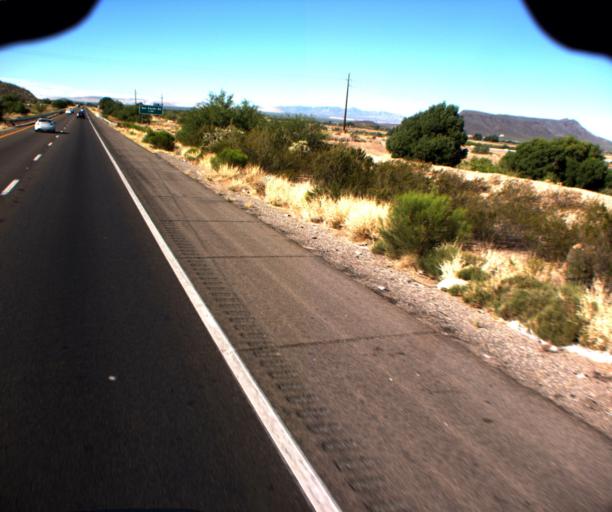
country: US
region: Arizona
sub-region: Pima County
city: Drexel Heights
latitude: 32.1221
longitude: -110.9883
